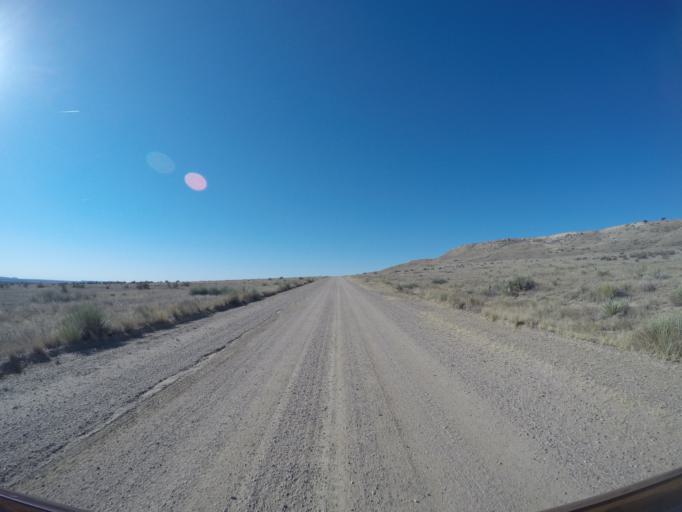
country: US
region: Colorado
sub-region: Otero County
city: La Junta
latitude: 37.7598
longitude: -103.5847
